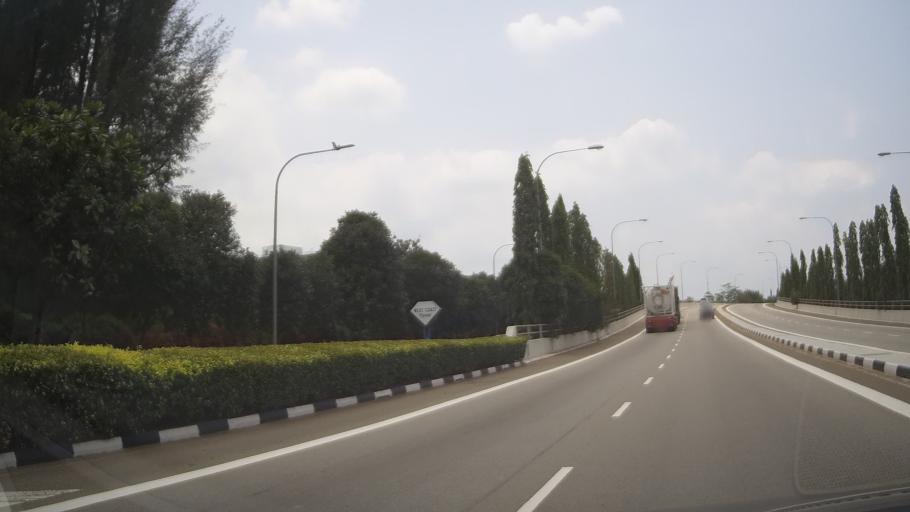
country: SG
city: Singapore
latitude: 1.2905
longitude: 103.7698
